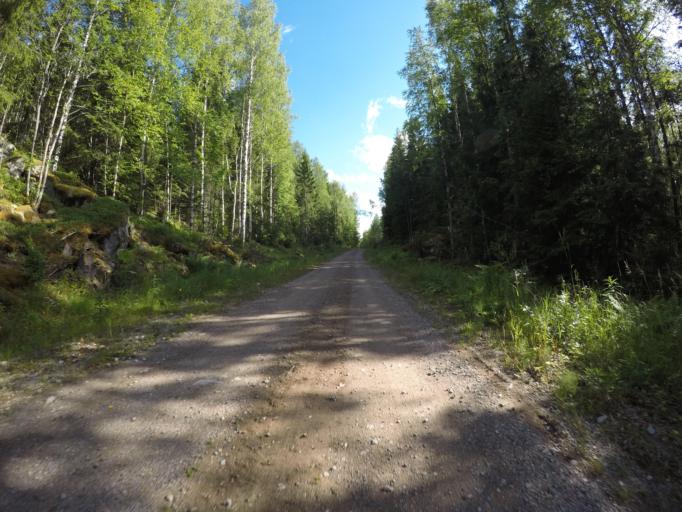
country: SE
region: OErebro
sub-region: Hallefors Kommun
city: Haellefors
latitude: 59.9954
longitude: 14.6057
